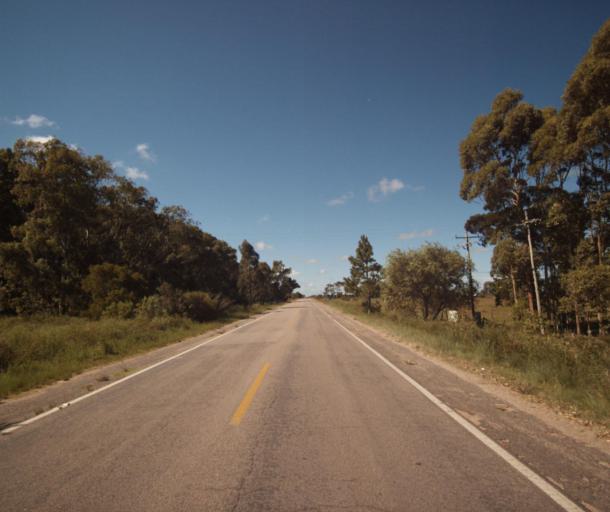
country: BR
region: Rio Grande do Sul
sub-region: Chui
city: Chui
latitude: -33.6620
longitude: -53.4362
